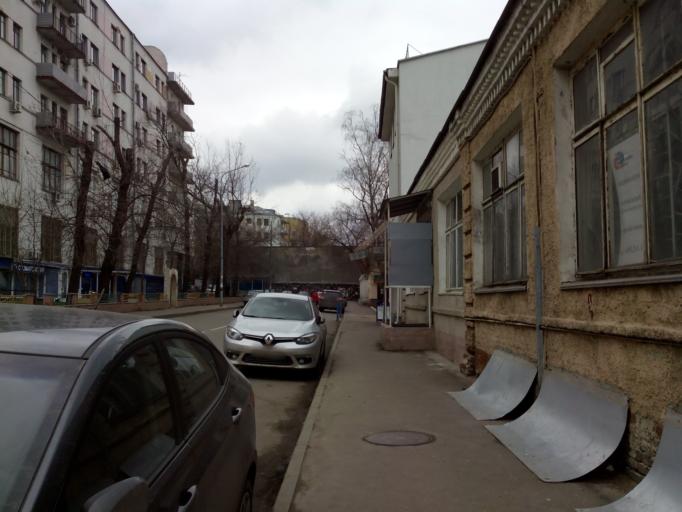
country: RU
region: Moskovskaya
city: Bogorodskoye
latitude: 55.7955
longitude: 37.7001
